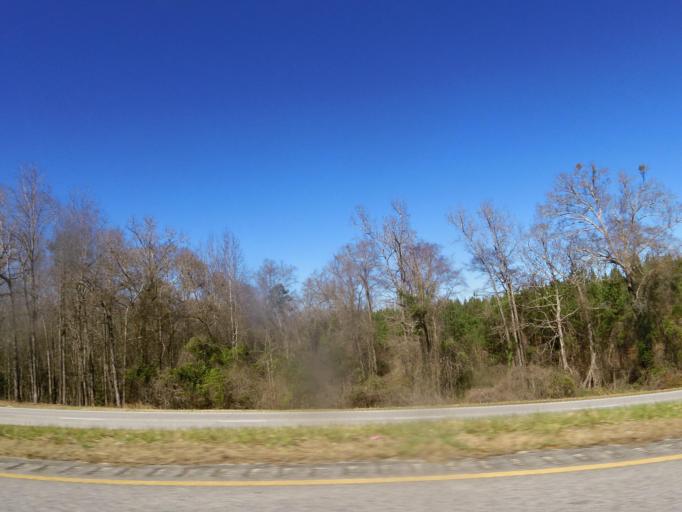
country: US
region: Alabama
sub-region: Bullock County
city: Union Springs
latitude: 32.1459
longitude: -85.6391
